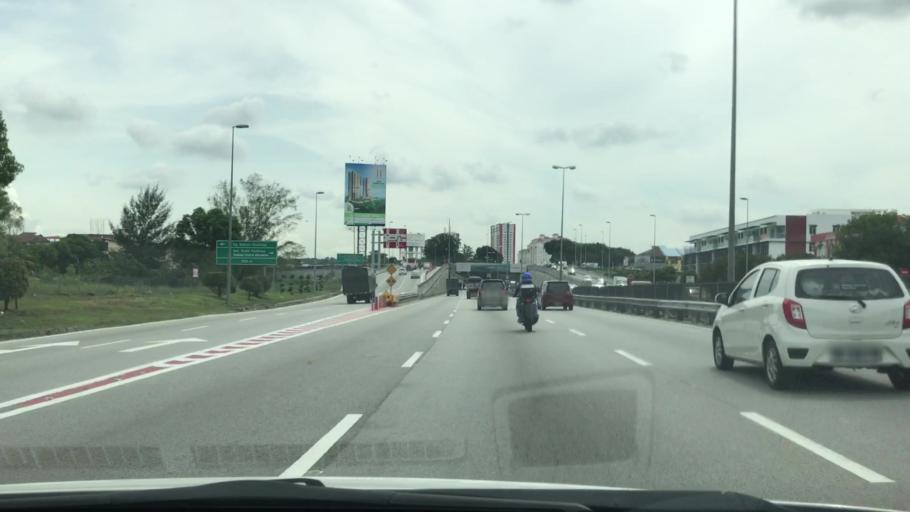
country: MY
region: Selangor
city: Subang Jaya
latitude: 2.9934
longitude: 101.6163
